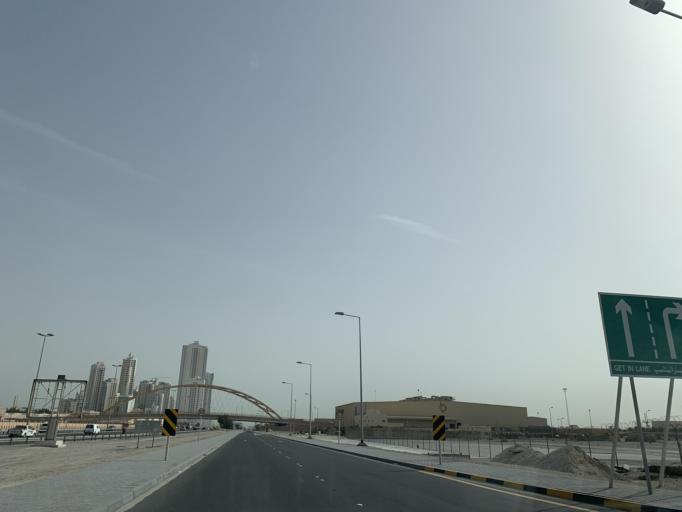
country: BH
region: Manama
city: Manama
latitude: 26.2048
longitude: 50.6120
